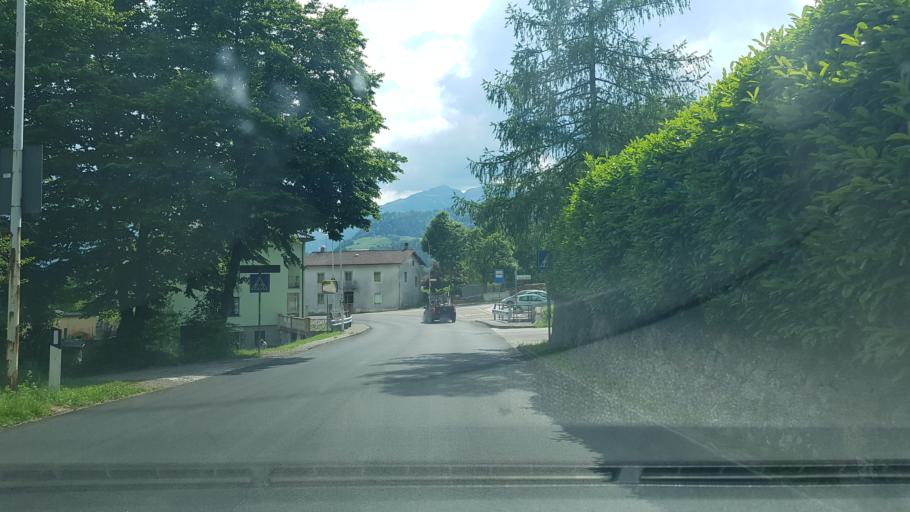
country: IT
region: Friuli Venezia Giulia
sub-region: Provincia di Udine
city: Zuglio
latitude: 46.4327
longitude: 13.0219
